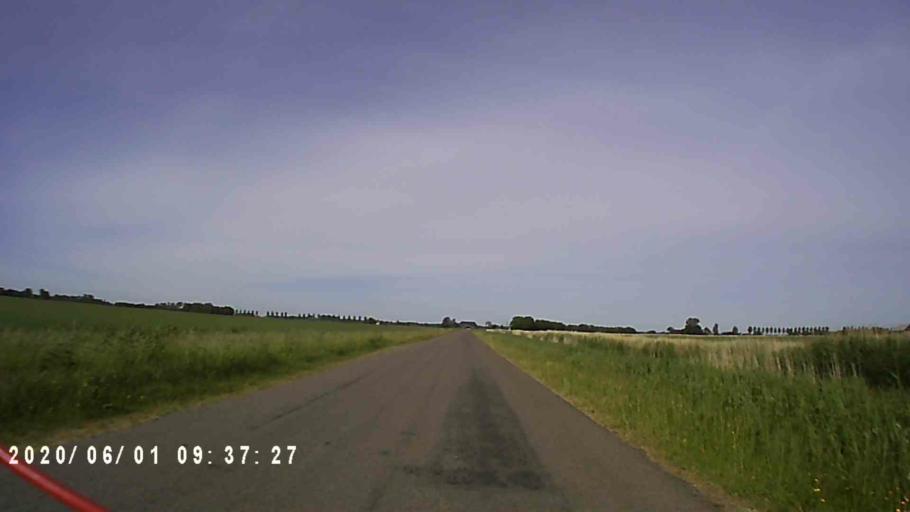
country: NL
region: Friesland
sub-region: Gemeente Het Bildt
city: Sint Annaparochie
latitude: 53.2585
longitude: 5.6918
